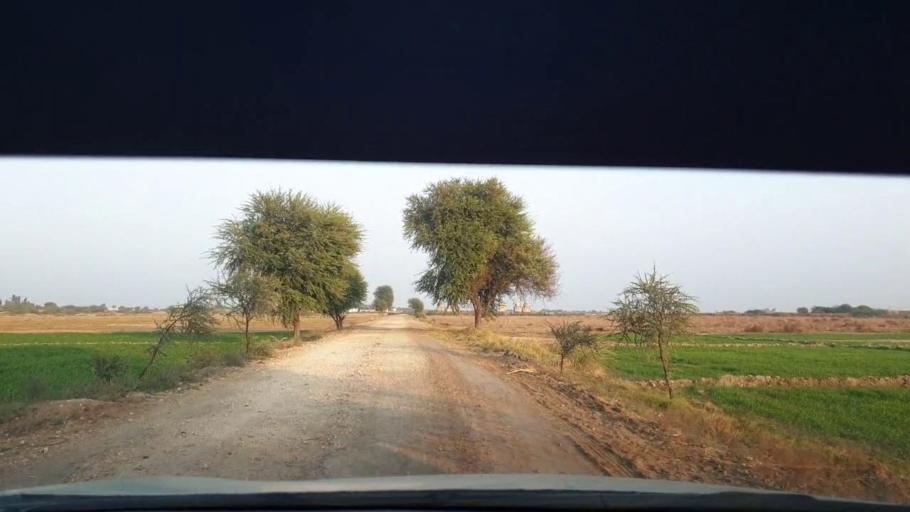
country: PK
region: Sindh
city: Berani
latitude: 25.7567
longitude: 68.9858
